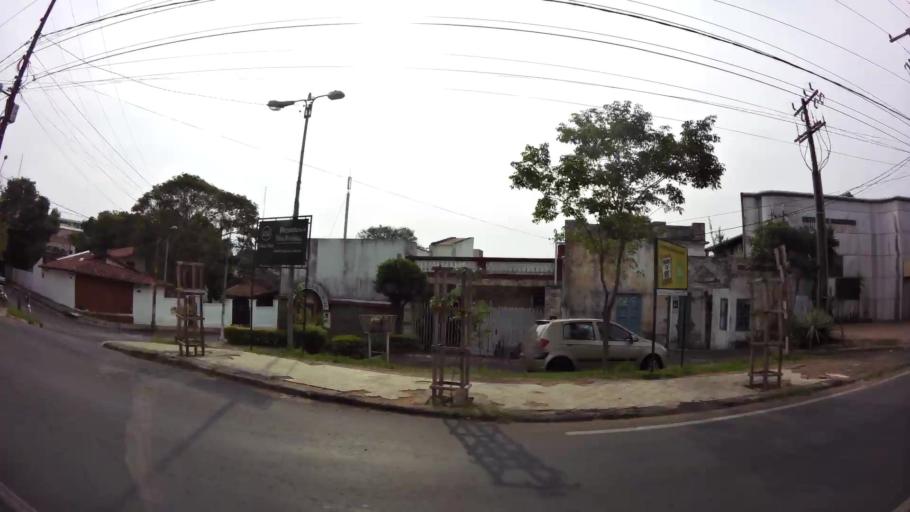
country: PY
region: Asuncion
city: Asuncion
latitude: -25.2973
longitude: -57.6122
